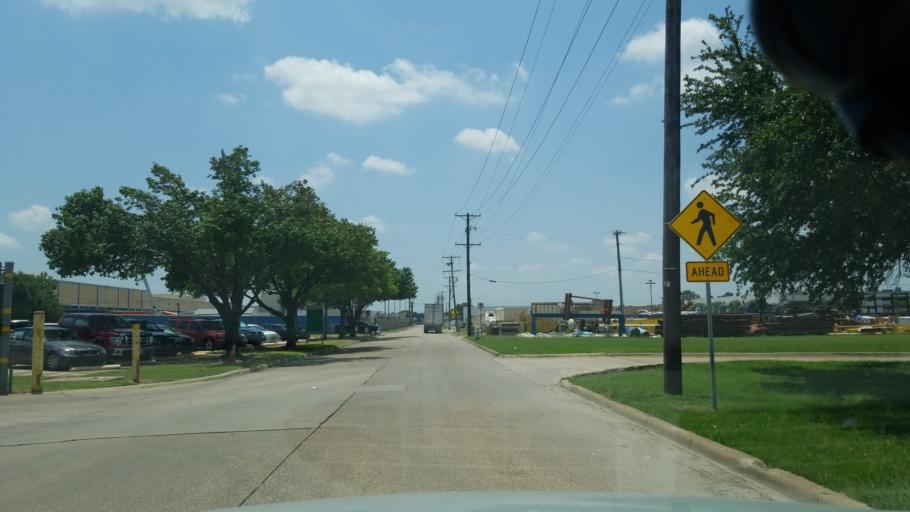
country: US
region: Texas
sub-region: Dallas County
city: Carrollton
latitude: 32.9572
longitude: -96.8642
